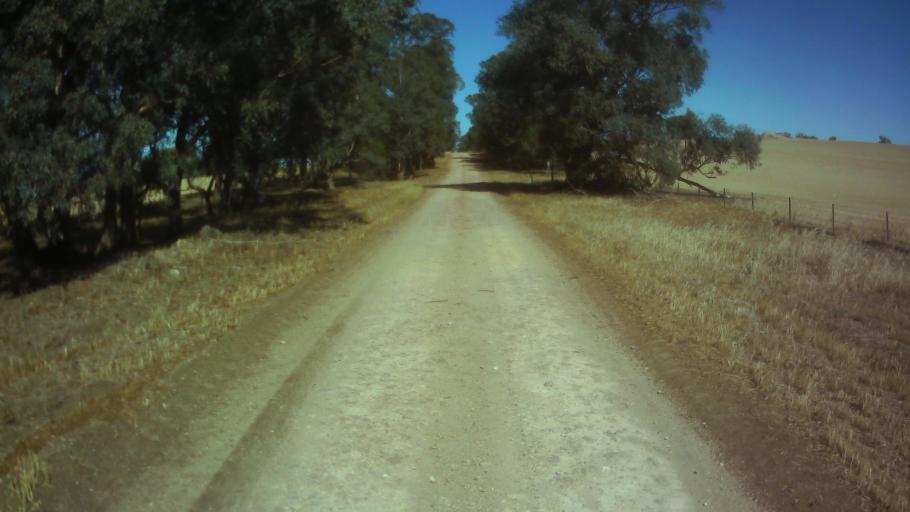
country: AU
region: New South Wales
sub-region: Weddin
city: Grenfell
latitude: -33.9938
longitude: 148.3550
